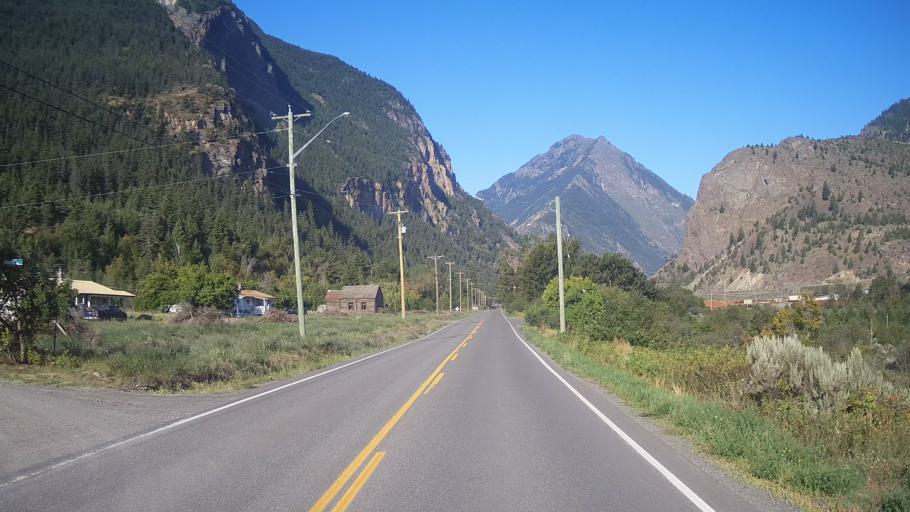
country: CA
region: British Columbia
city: Lillooet
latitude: 50.6729
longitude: -121.9399
